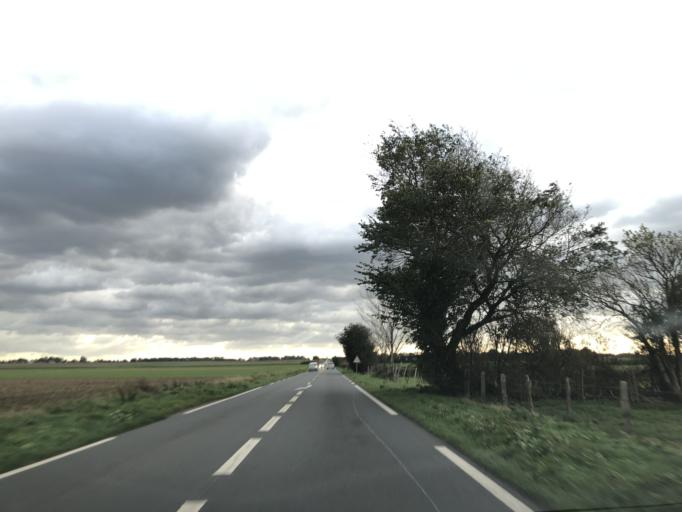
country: FR
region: Picardie
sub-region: Departement de la Somme
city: Ault
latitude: 50.0931
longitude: 1.4603
